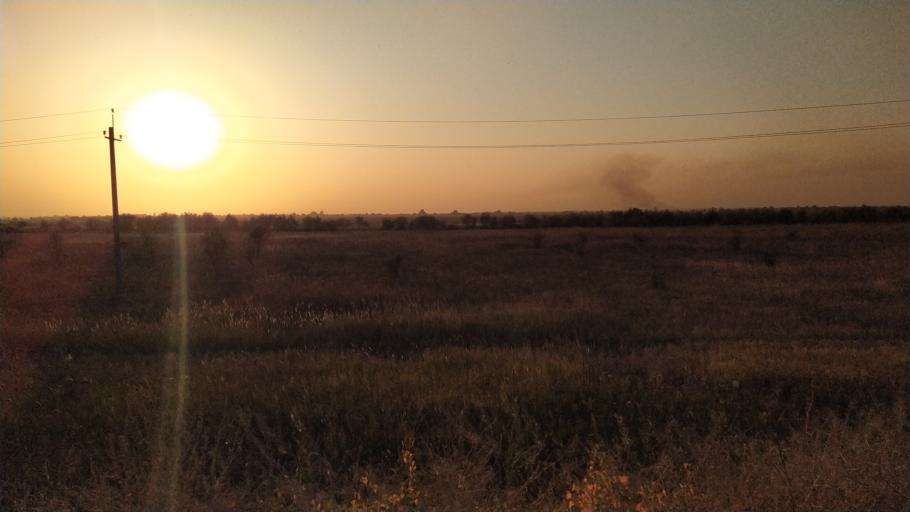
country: RU
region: Rostov
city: Kuleshovka
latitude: 47.1412
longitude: 39.6446
